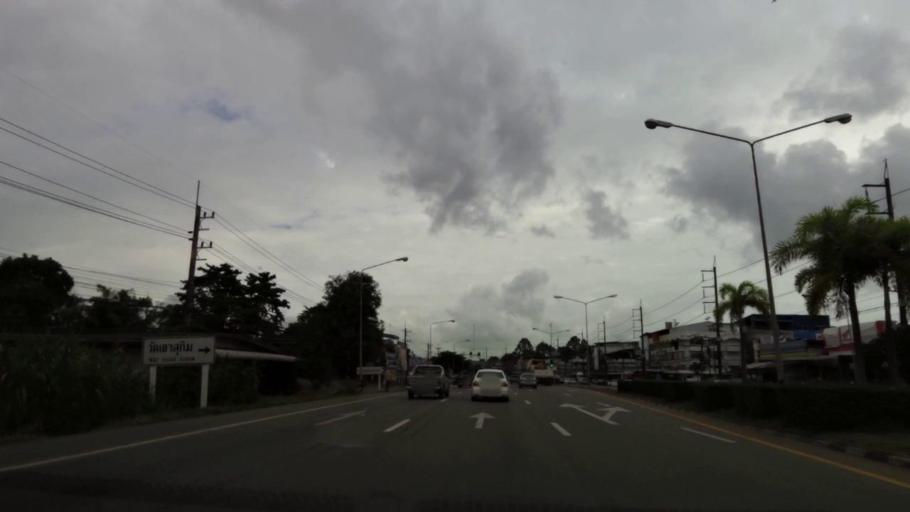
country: TH
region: Chanthaburi
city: Tha Mai
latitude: 12.7203
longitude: 101.9737
